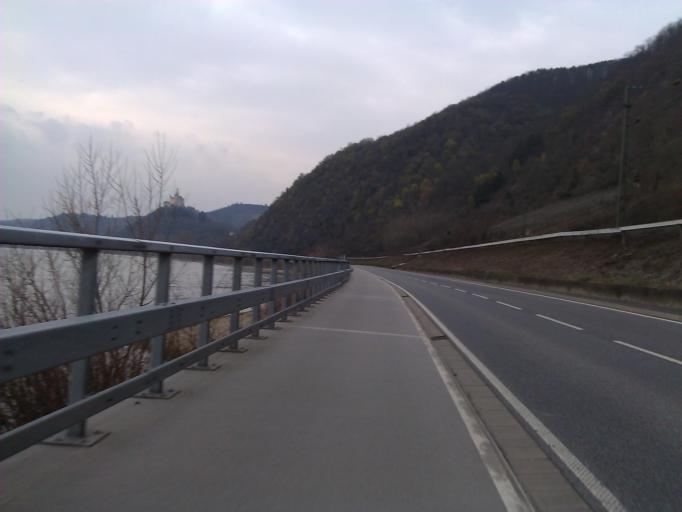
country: DE
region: Rheinland-Pfalz
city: Spay
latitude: 50.2563
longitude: 7.6545
